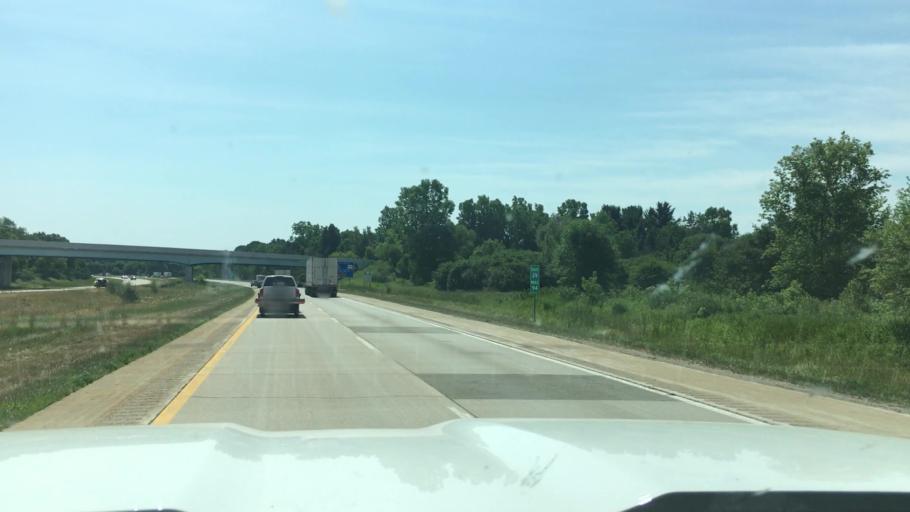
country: US
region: Michigan
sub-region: Clinton County
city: Bath
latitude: 42.7870
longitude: -84.4203
